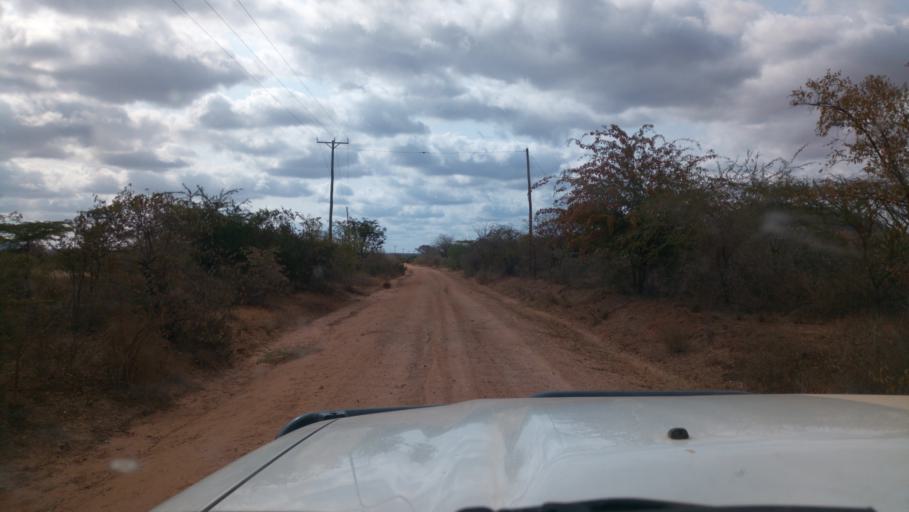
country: KE
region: Kitui
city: Kitui
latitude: -1.9885
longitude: 38.3275
